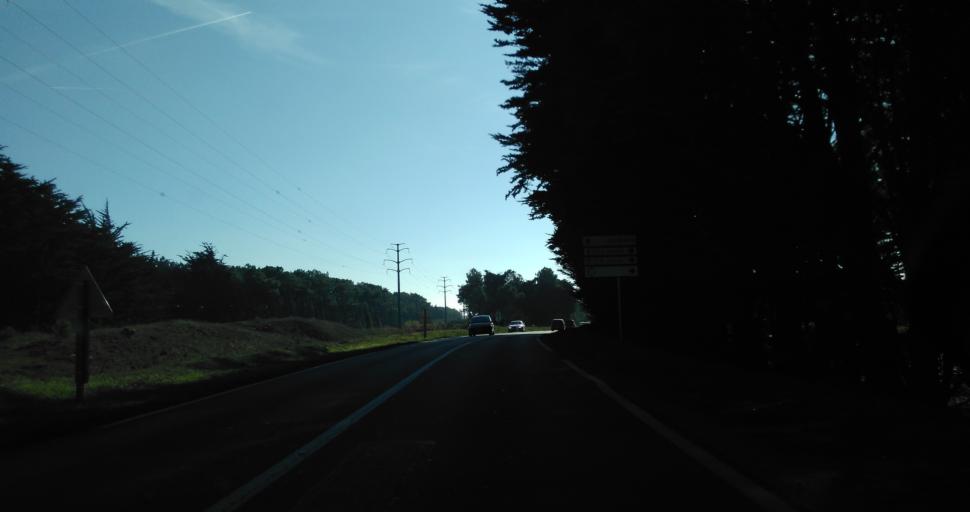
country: FR
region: Brittany
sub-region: Departement du Morbihan
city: Plouharnel
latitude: 47.5937
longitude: -3.1320
